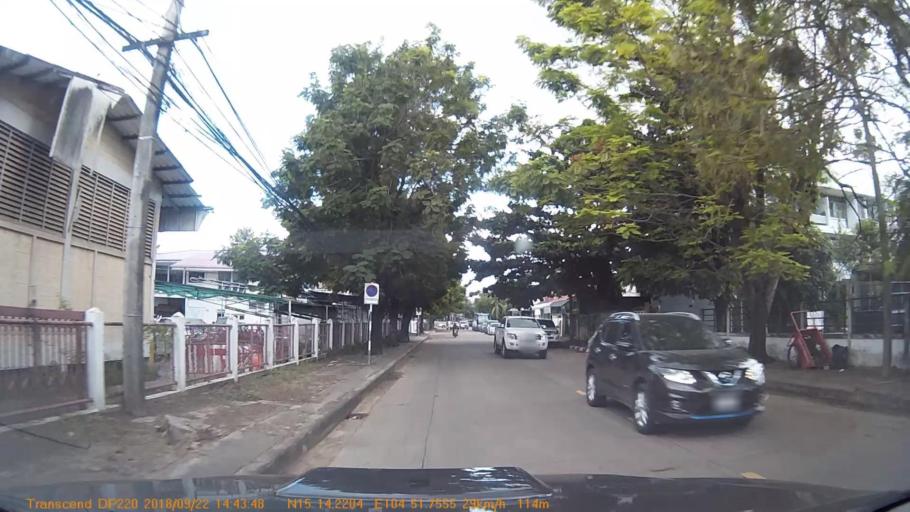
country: TH
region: Changwat Ubon Ratchathani
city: Ubon Ratchathani
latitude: 15.2368
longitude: 104.8626
